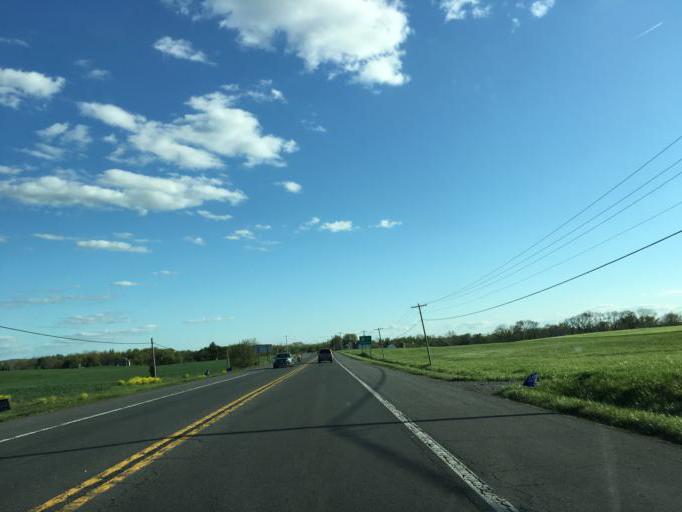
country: US
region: Maryland
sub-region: Frederick County
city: Walkersville
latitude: 39.4601
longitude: -77.3657
